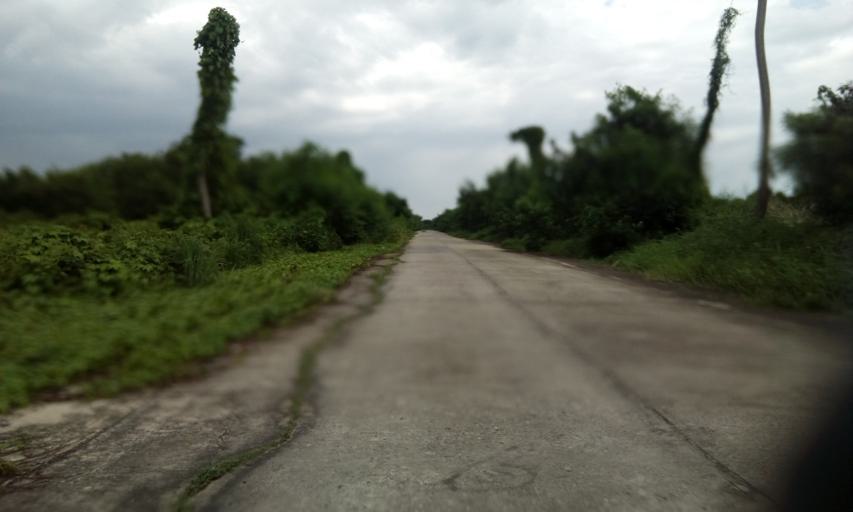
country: TH
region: Pathum Thani
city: Nong Suea
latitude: 14.0646
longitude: 100.8353
